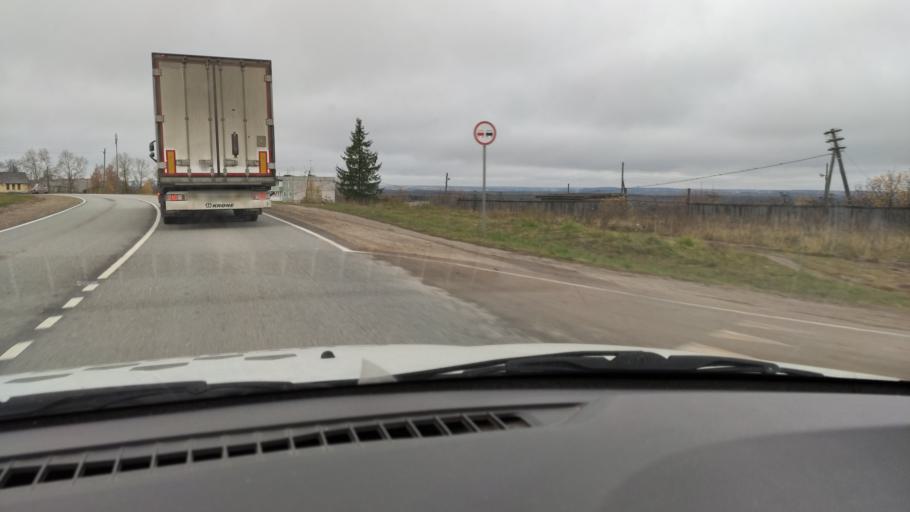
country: RU
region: Kirov
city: Slobodskoy
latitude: 58.7504
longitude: 50.3137
